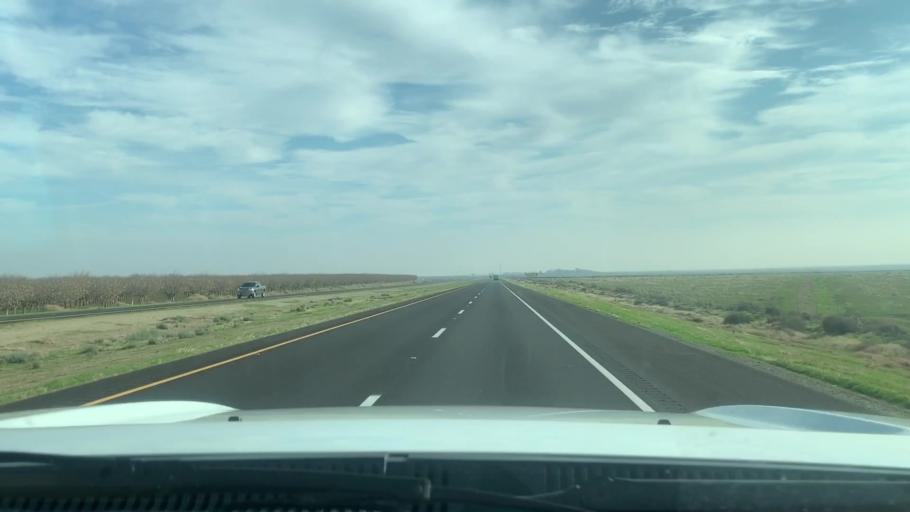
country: US
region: California
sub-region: Kern County
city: Lost Hills
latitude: 35.6146
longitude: -119.8917
